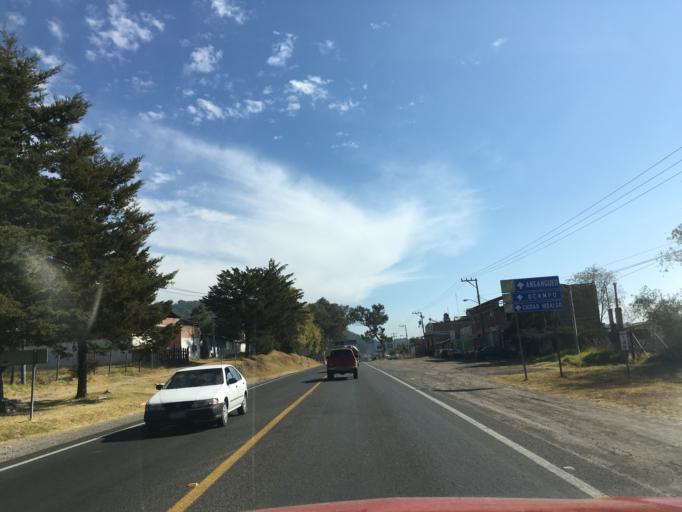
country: MX
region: Michoacan
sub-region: Hidalgo
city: Colonia Ecologica Asociacion de Lucha Social (Lucha Social)
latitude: 19.6986
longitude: -100.6009
